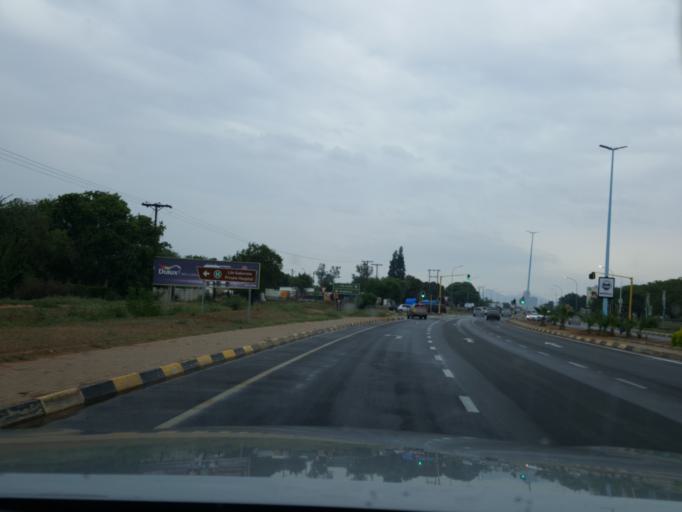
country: BW
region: South East
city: Gaborone
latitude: -24.6217
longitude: 25.9306
